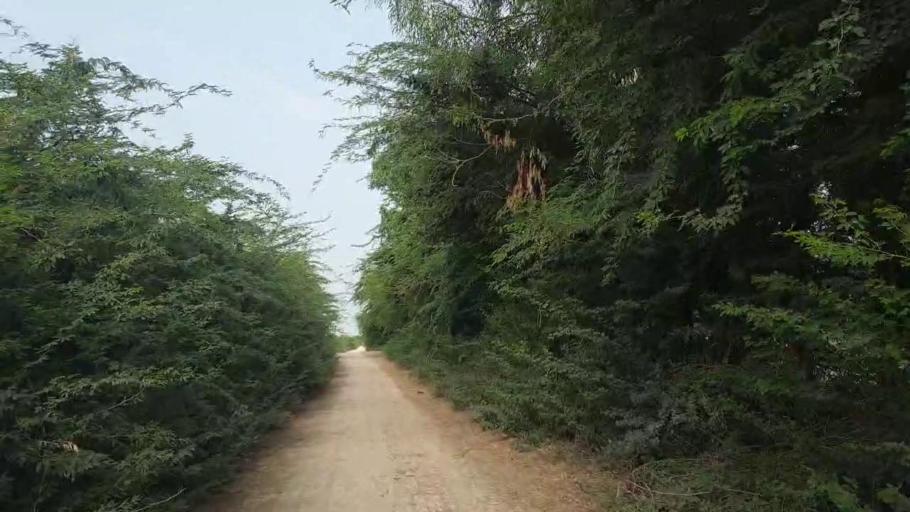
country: PK
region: Sindh
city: Badin
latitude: 24.5993
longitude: 68.7413
